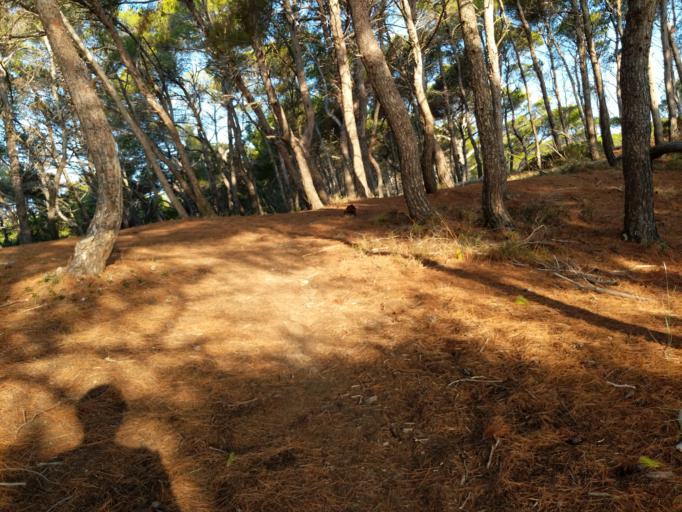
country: IT
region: Apulia
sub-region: Provincia di Foggia
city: Isole Tremiti
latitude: 42.1157
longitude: 15.4955
